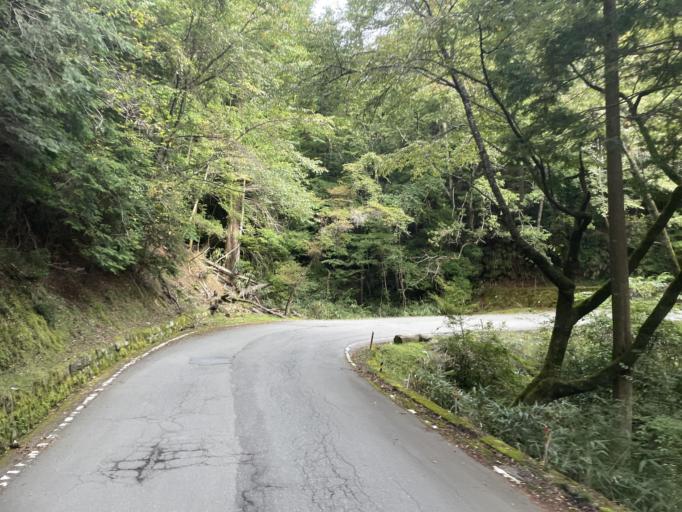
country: JP
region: Wakayama
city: Koya
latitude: 34.2234
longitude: 135.5750
